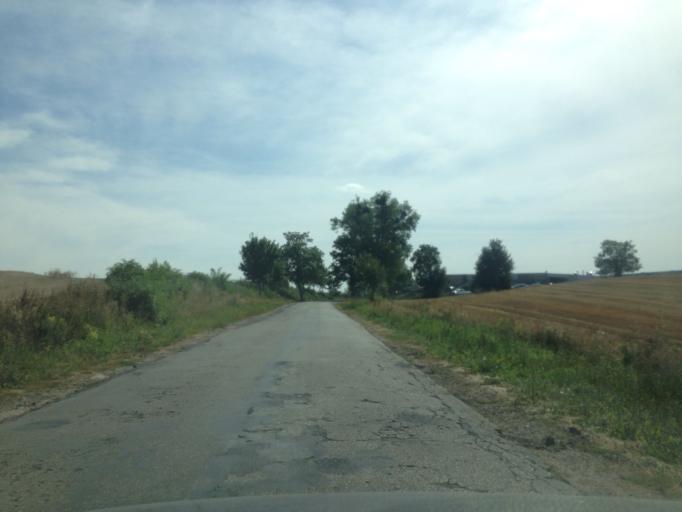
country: PL
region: Kujawsko-Pomorskie
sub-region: Powiat brodnicki
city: Swiedziebnia
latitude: 53.2202
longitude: 19.5136
